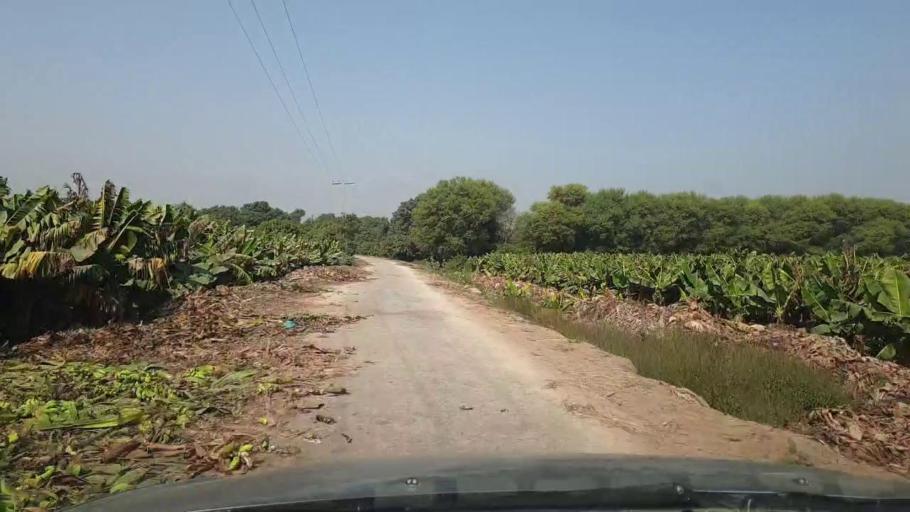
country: PK
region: Sindh
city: Tando Jam
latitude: 25.3616
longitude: 68.5157
